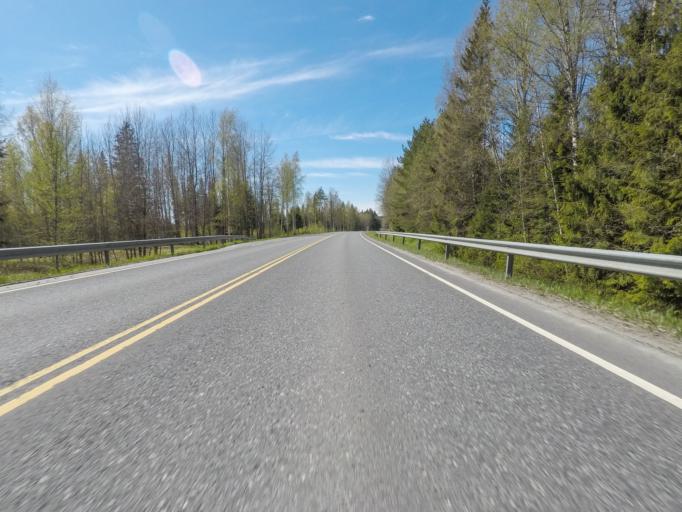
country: FI
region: Haeme
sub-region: Forssa
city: Humppila
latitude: 60.9804
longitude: 23.4370
